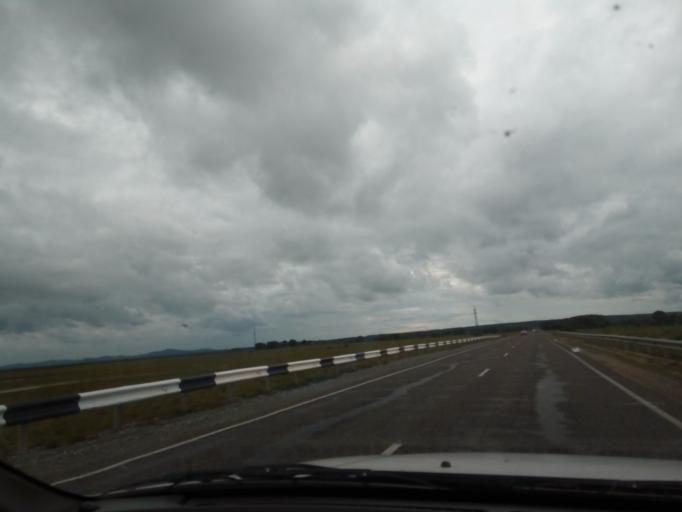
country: RU
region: Primorskiy
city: Dal'nerechensk
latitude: 45.9120
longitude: 133.7649
